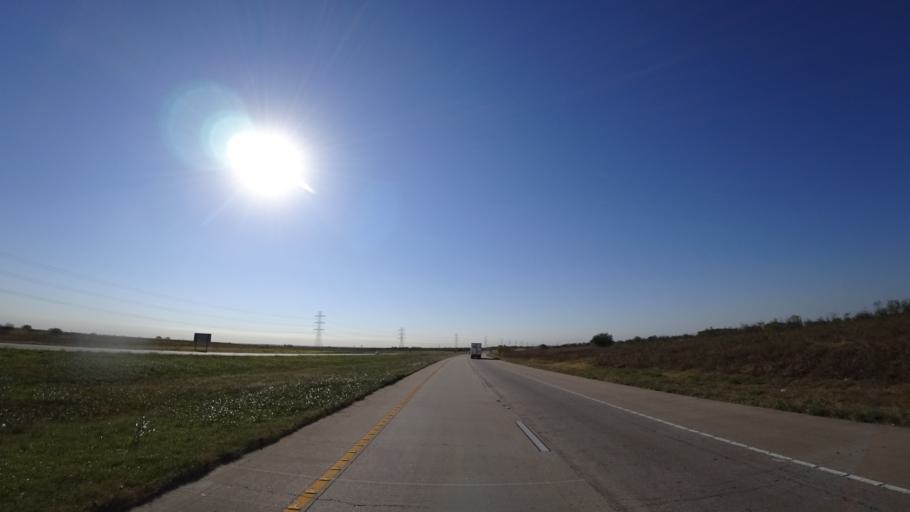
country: US
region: Texas
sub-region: Travis County
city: Manor
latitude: 30.3927
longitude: -97.5793
